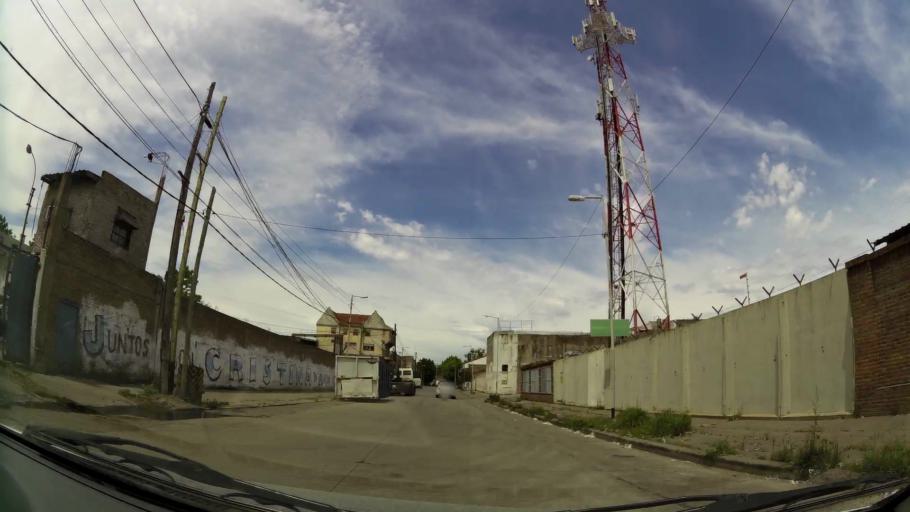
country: AR
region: Buenos Aires
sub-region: Partido de Avellaneda
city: Avellaneda
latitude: -34.6654
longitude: -58.3870
